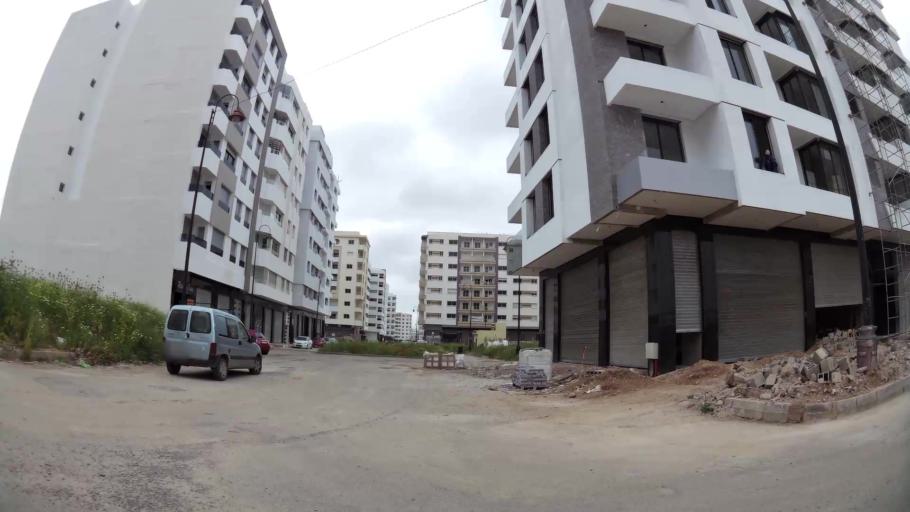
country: MA
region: Fes-Boulemane
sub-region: Fes
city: Fes
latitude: 34.0357
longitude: -5.0147
